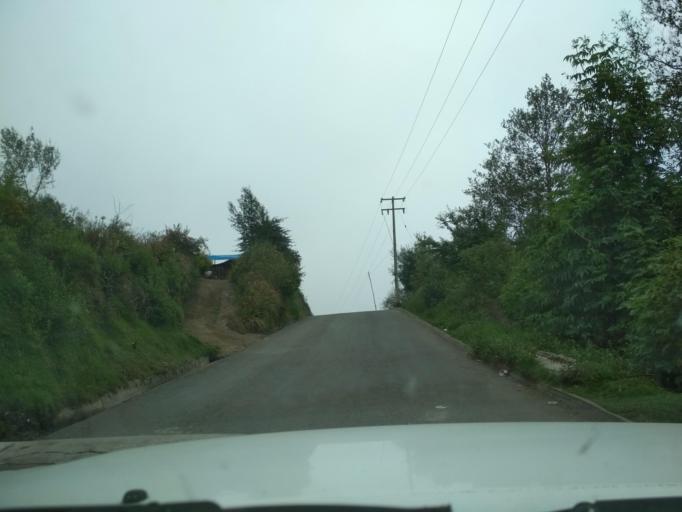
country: MX
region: Veracruz
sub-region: La Perla
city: Chilapa
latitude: 18.9756
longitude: -97.1927
